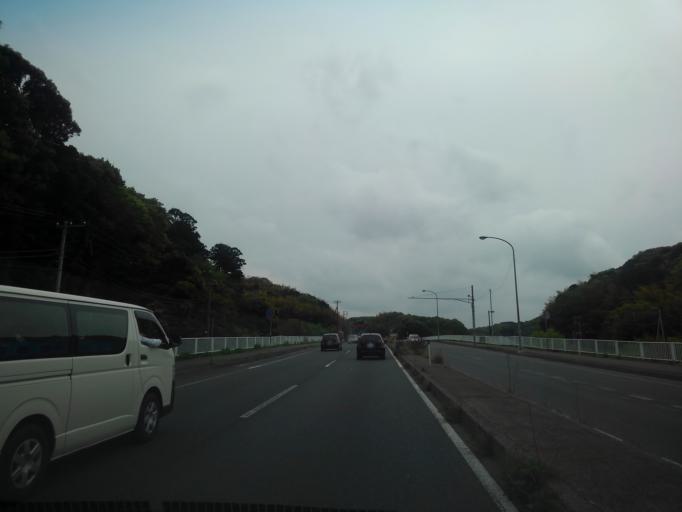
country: JP
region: Chiba
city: Kisarazu
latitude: 35.3550
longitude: 139.9206
